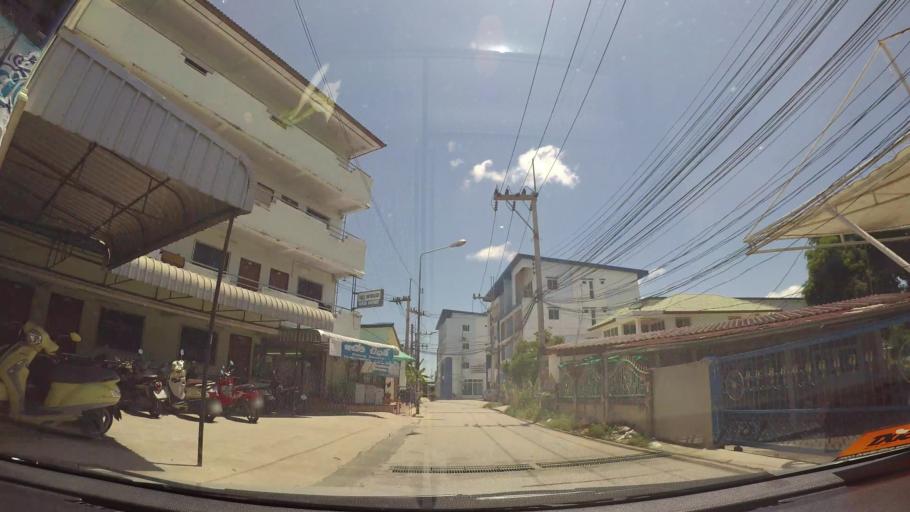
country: TH
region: Chon Buri
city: Phatthaya
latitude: 12.9224
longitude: 100.8917
